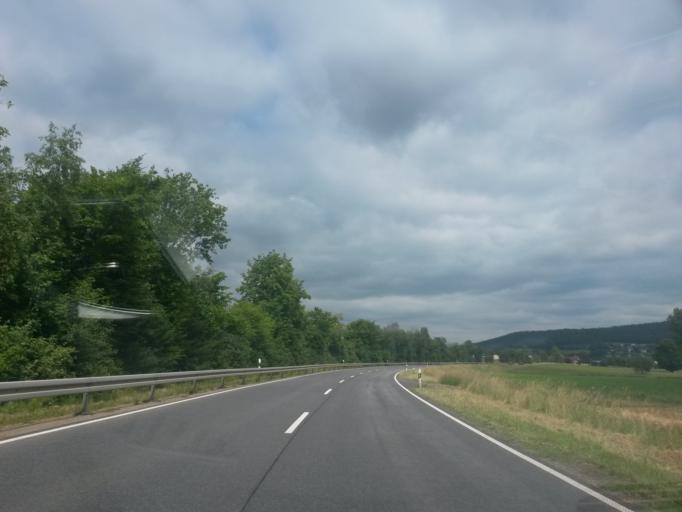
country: DE
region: Hesse
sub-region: Regierungsbezirk Kassel
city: Niederaula
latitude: 50.8269
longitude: 9.6525
